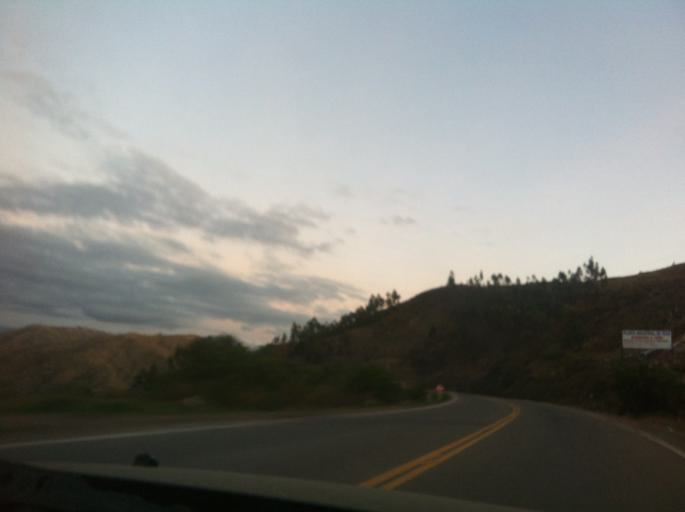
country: BO
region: Cochabamba
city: Irpa Irpa
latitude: -17.6604
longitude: -66.4062
